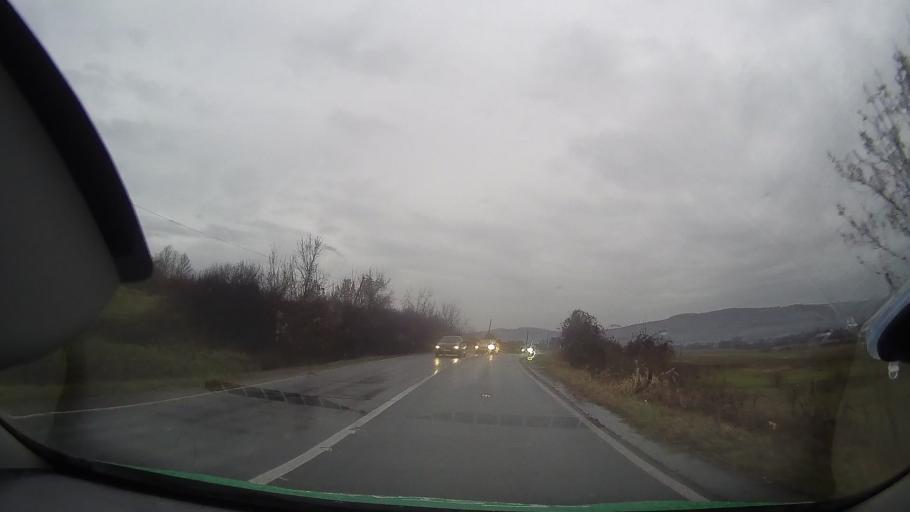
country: RO
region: Bihor
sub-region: Comuna Rabagani
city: Rabagani
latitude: 46.7400
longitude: 22.2293
